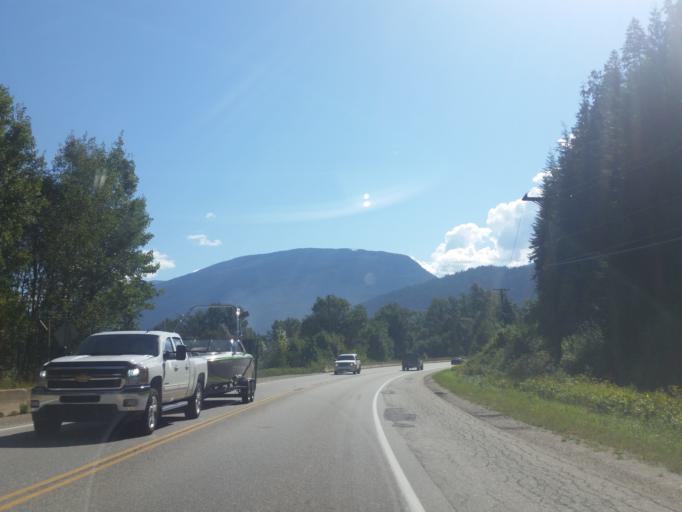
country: CA
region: British Columbia
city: Sicamous
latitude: 50.8918
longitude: -118.8662
